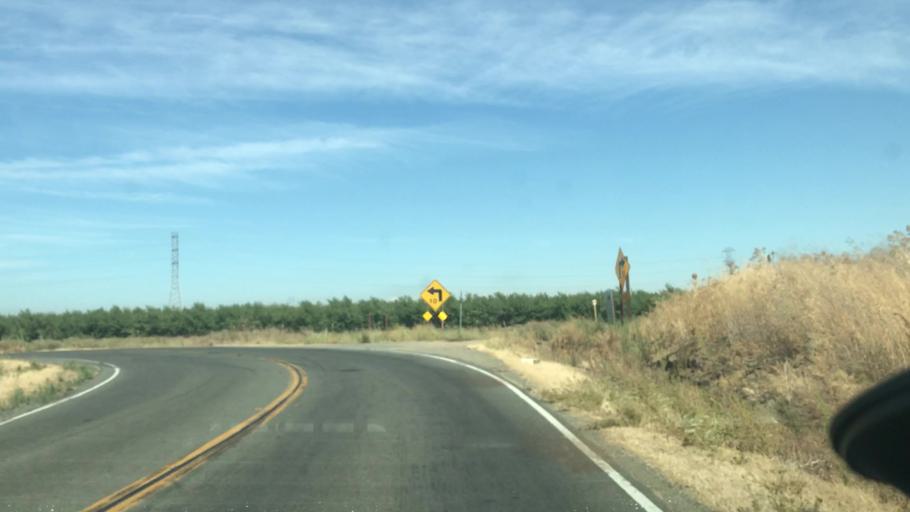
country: US
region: California
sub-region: Solano County
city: Vacaville
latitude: 38.3083
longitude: -121.9160
